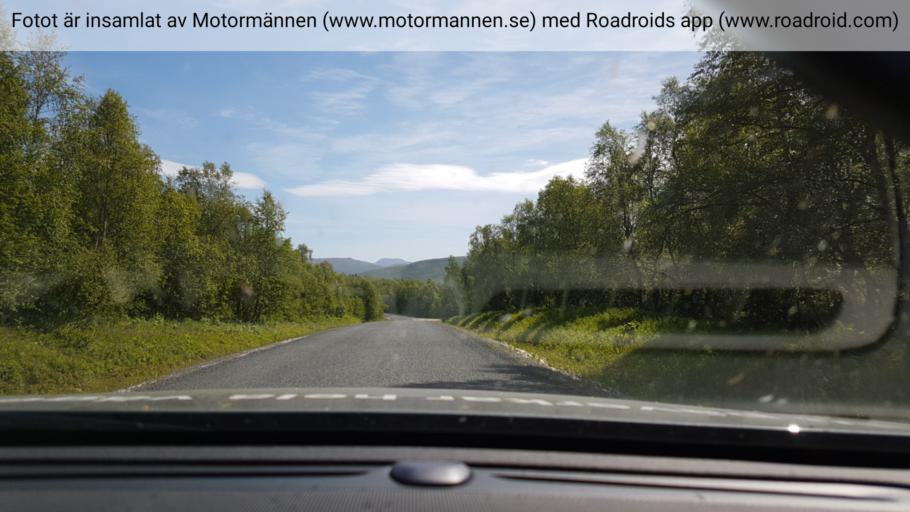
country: NO
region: Nordland
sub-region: Hattfjelldal
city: Hattfjelldal
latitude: 65.3345
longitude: 15.1321
